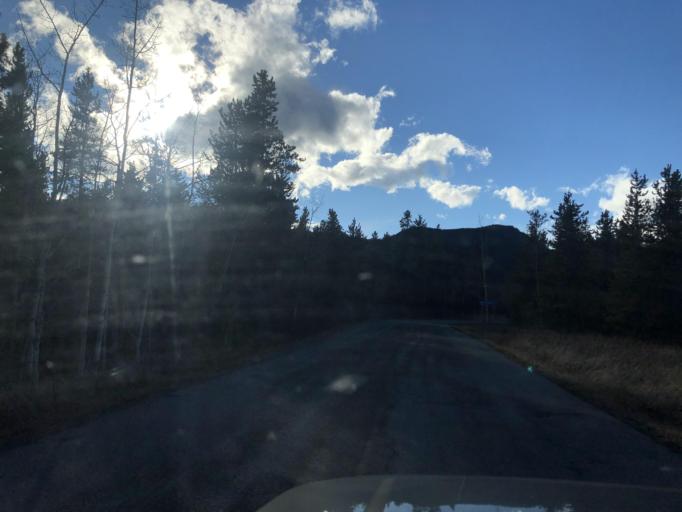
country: CA
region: Alberta
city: Canmore
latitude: 51.0714
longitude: -115.0783
